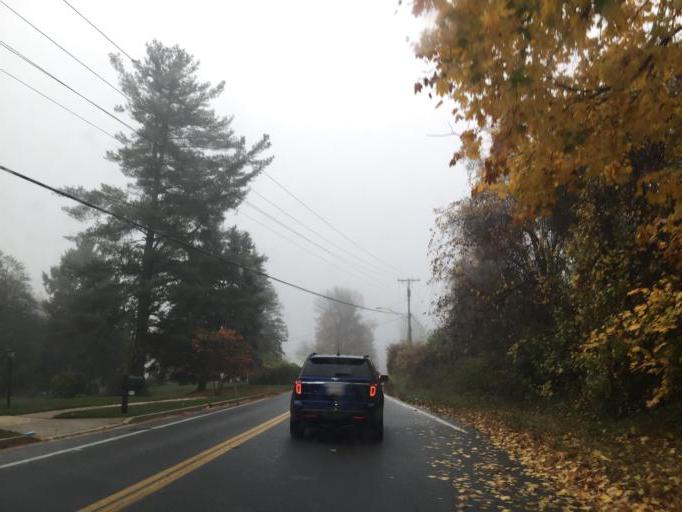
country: US
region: Maryland
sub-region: Baltimore County
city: Randallstown
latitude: 39.3622
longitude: -76.7922
